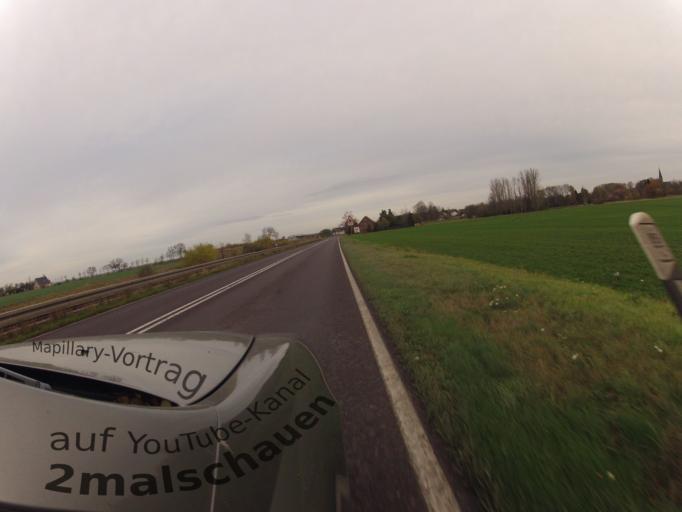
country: DE
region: Saxony-Anhalt
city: Konnern
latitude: 51.7021
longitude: 11.7639
